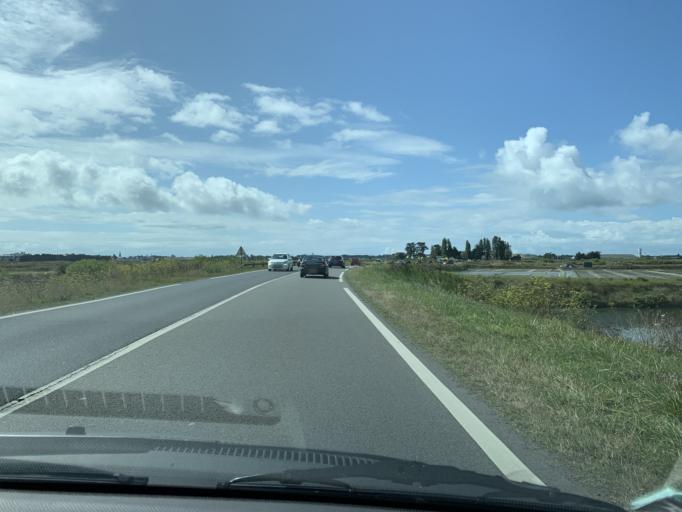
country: FR
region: Pays de la Loire
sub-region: Departement de la Loire-Atlantique
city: Le Pouliguen
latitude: 47.2951
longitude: -2.4357
